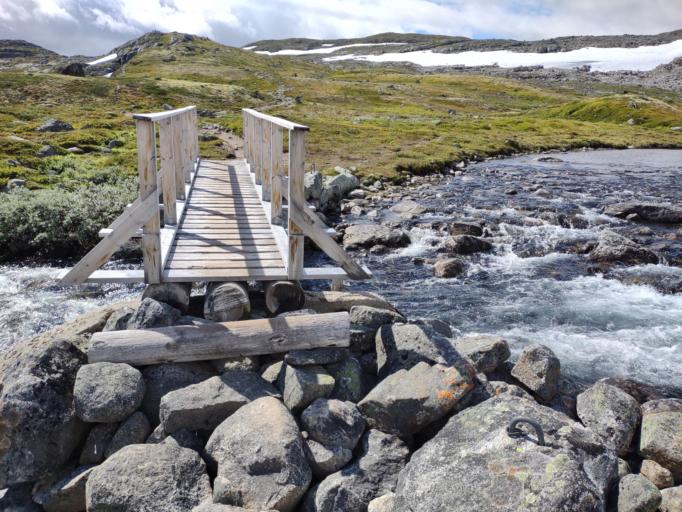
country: NO
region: Buskerud
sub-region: Hol
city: Geilo
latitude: 60.4498
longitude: 7.7019
